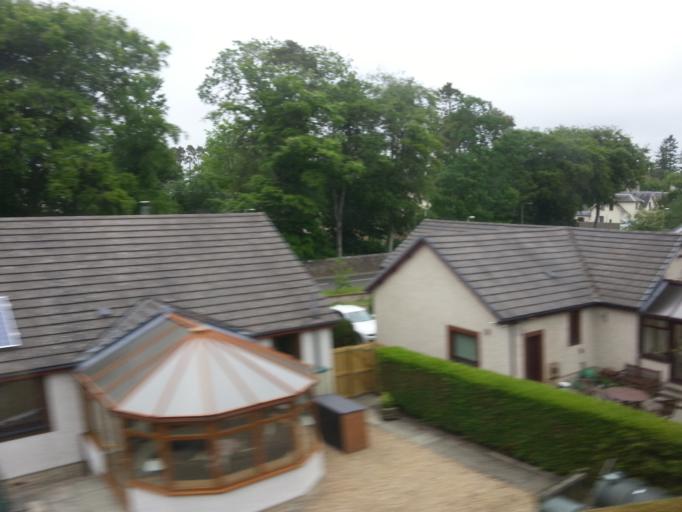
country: GB
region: Scotland
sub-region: Perth and Kinross
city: Stanley
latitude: 56.5274
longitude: -3.4609
